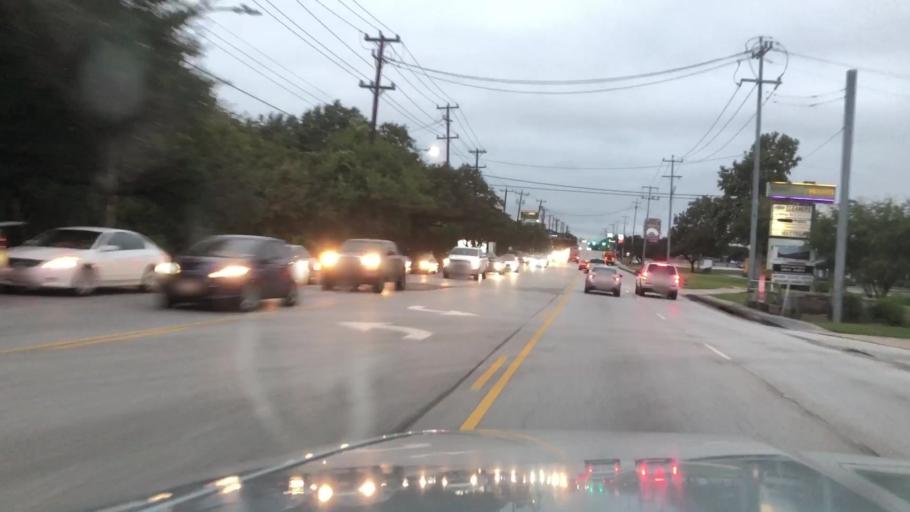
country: US
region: Texas
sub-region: Bexar County
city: Shavano Park
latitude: 29.5631
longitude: -98.5965
